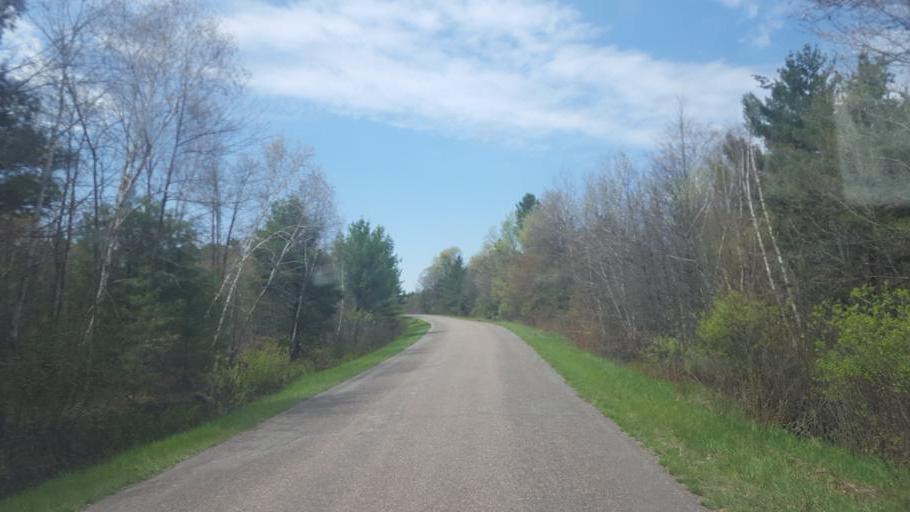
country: US
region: Wisconsin
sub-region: Clark County
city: Neillsville
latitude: 44.2892
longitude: -90.4917
